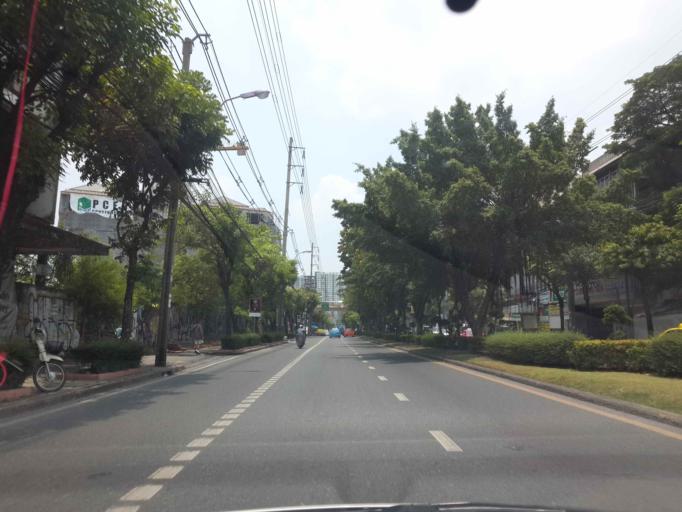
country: TH
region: Bangkok
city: Khlong Toei
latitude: 13.7157
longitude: 100.5749
